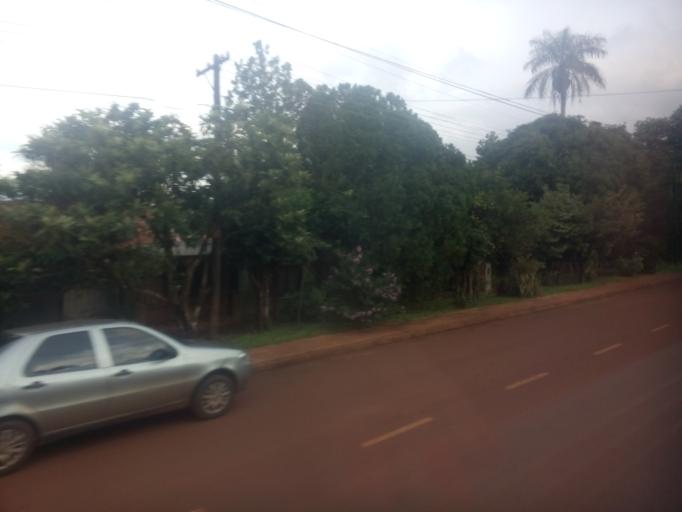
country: AR
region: Misiones
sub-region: Departamento de Obera
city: Obera
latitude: -27.4953
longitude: -55.1435
